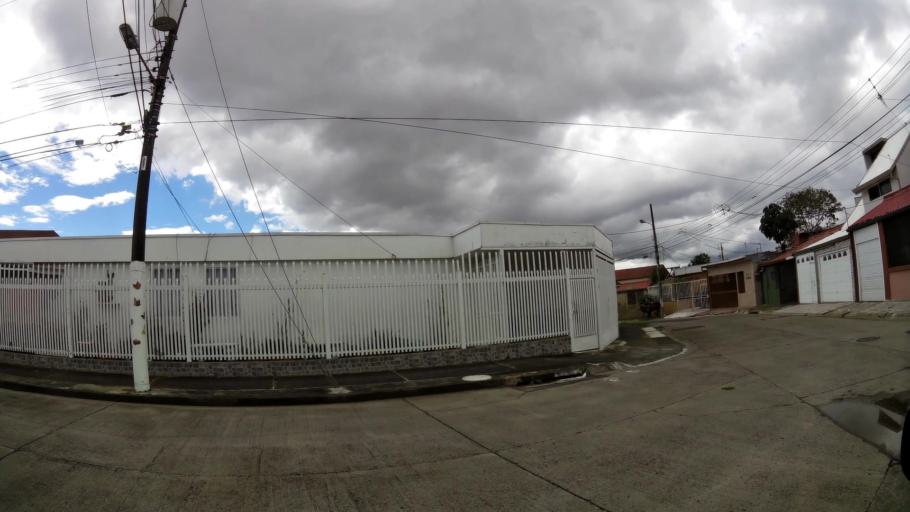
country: CR
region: San Jose
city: Curridabat
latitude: 9.9203
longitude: -84.0405
